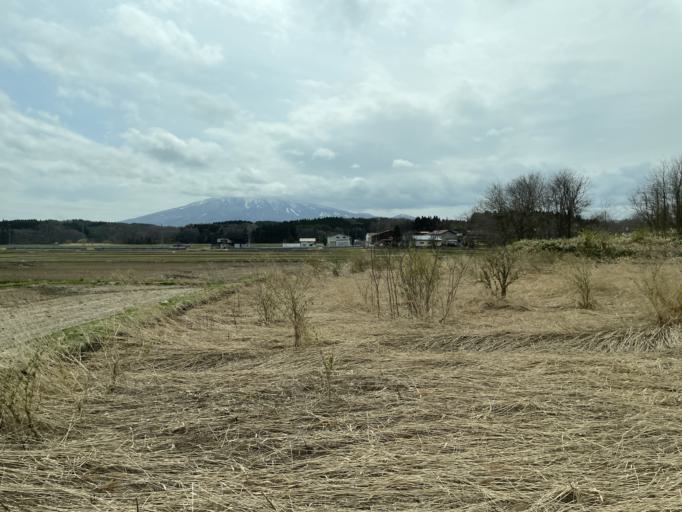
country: JP
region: Aomori
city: Shimokizukuri
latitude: 40.7860
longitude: 140.3107
